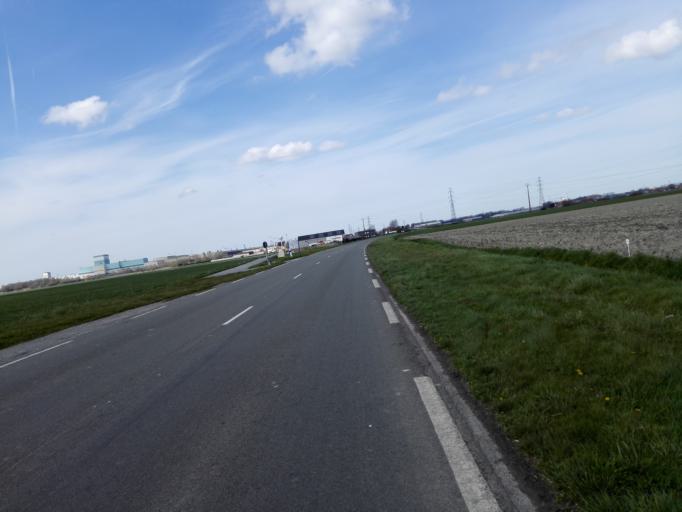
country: FR
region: Nord-Pas-de-Calais
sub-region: Departement du Nord
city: Spycker
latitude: 50.9776
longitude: 2.3085
